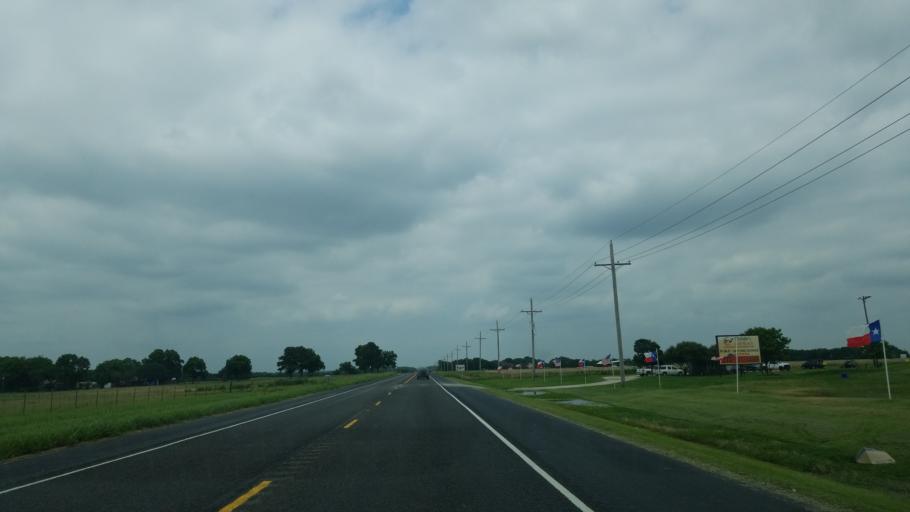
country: US
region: Texas
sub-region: Denton County
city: Pilot Point
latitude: 33.4219
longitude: -96.9365
